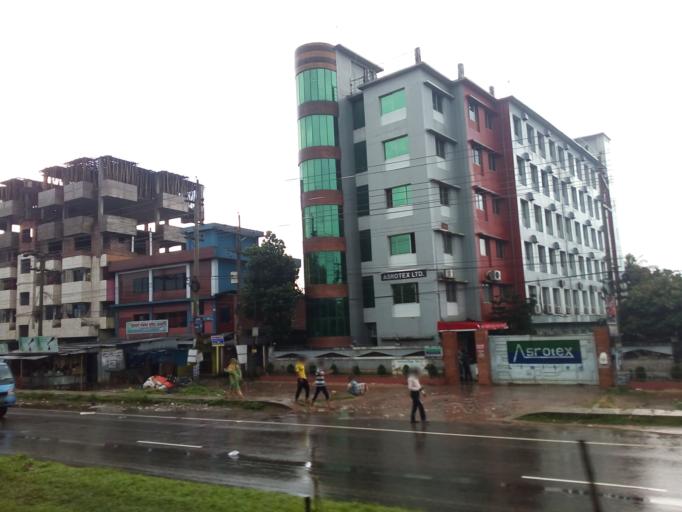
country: BD
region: Dhaka
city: Gafargaon
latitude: 24.1781
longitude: 90.4274
